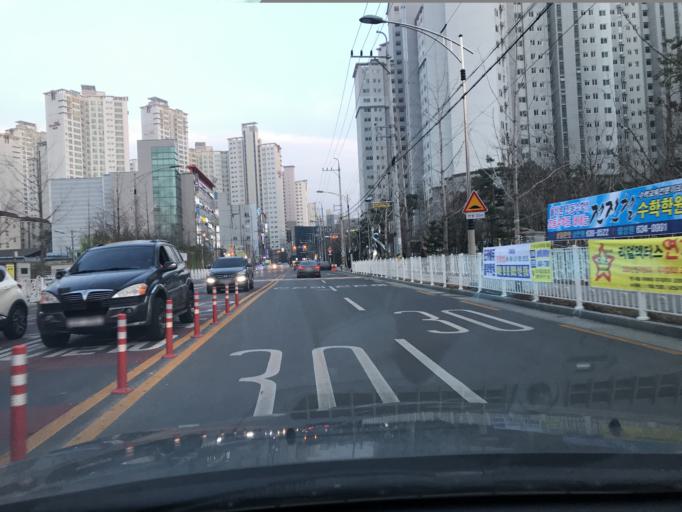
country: KR
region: Daegu
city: Hwawon
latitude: 35.8166
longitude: 128.5180
